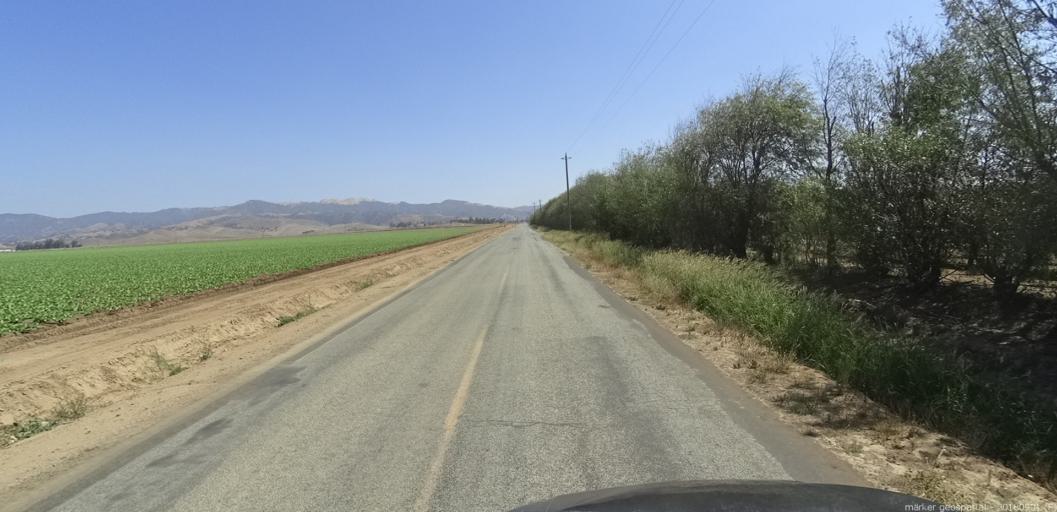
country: US
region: California
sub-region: Monterey County
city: Chualar
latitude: 36.5805
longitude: -121.4834
